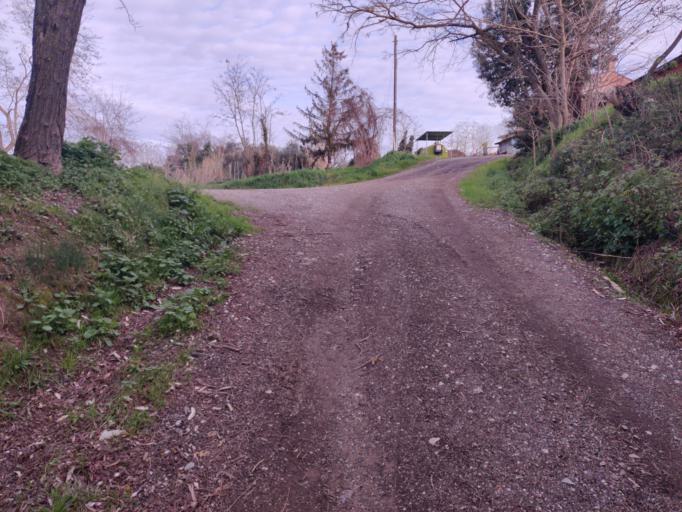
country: IT
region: Tuscany
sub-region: Province of Pisa
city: Palaia
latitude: 43.5407
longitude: 10.7921
